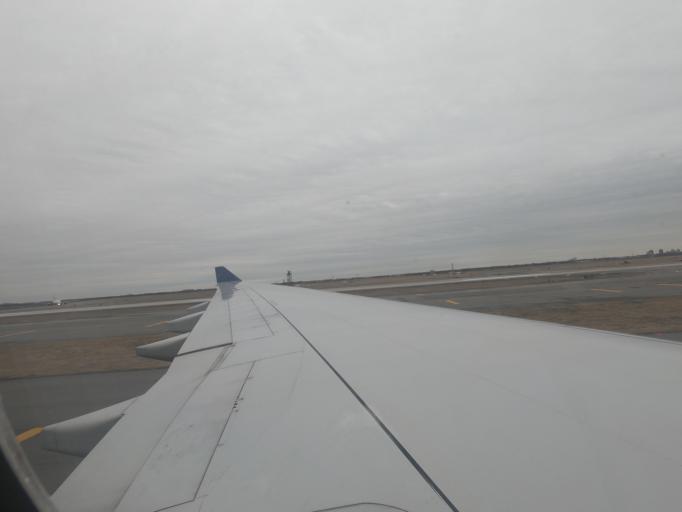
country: US
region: New York
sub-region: Nassau County
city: Inwood
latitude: 40.6414
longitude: -73.7731
